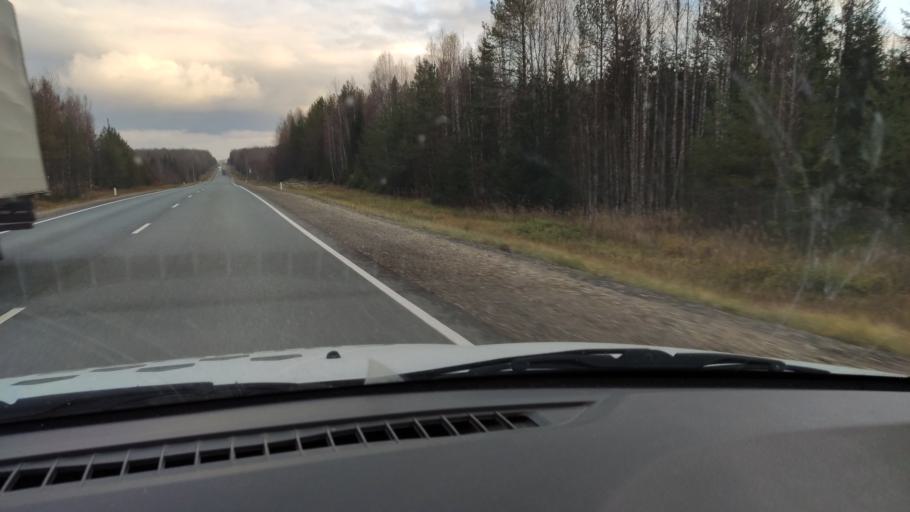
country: RU
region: Kirov
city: Chernaya Kholunitsa
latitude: 58.8080
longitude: 51.8427
